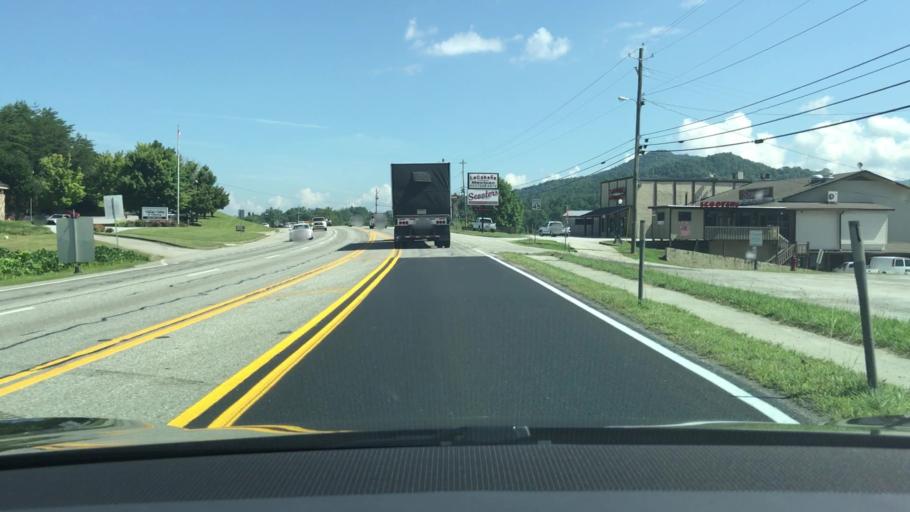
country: US
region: Georgia
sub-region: Rabun County
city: Mountain City
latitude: 34.9754
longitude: -83.3837
